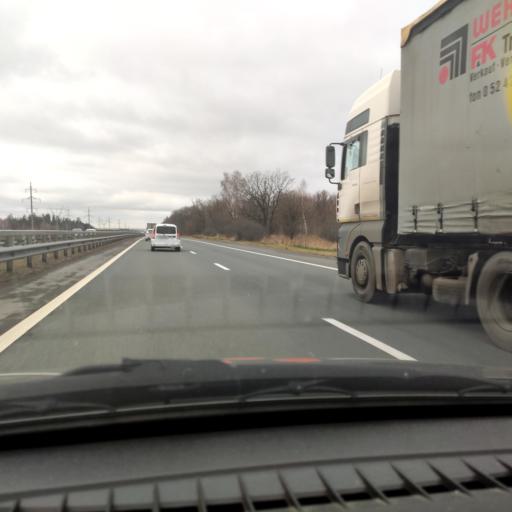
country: RU
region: Samara
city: Pribrezhnyy
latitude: 53.5185
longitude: 49.7989
